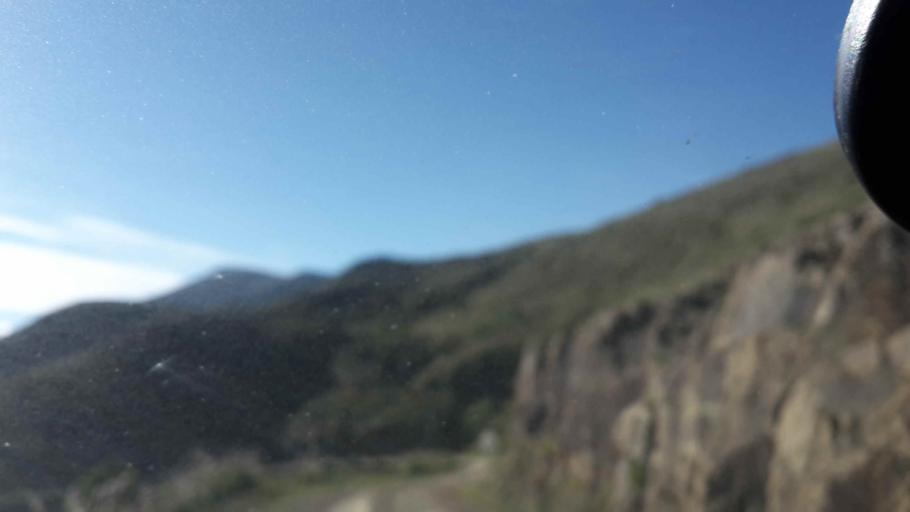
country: BO
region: Cochabamba
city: Arani
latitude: -17.7361
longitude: -65.6228
